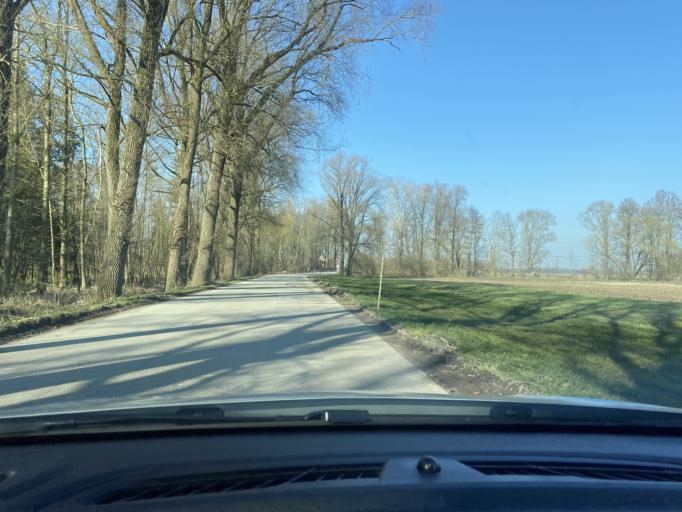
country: DE
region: Bavaria
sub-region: Upper Bavaria
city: Moosinning
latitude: 48.2848
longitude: 11.8304
